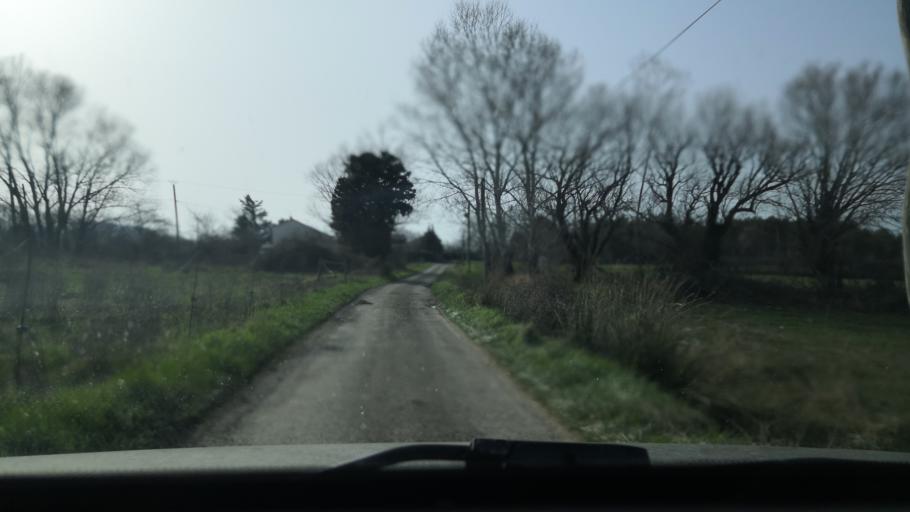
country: FR
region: Rhone-Alpes
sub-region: Departement de la Drome
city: La Begude-de-Mazenc
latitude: 44.5390
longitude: 4.9220
